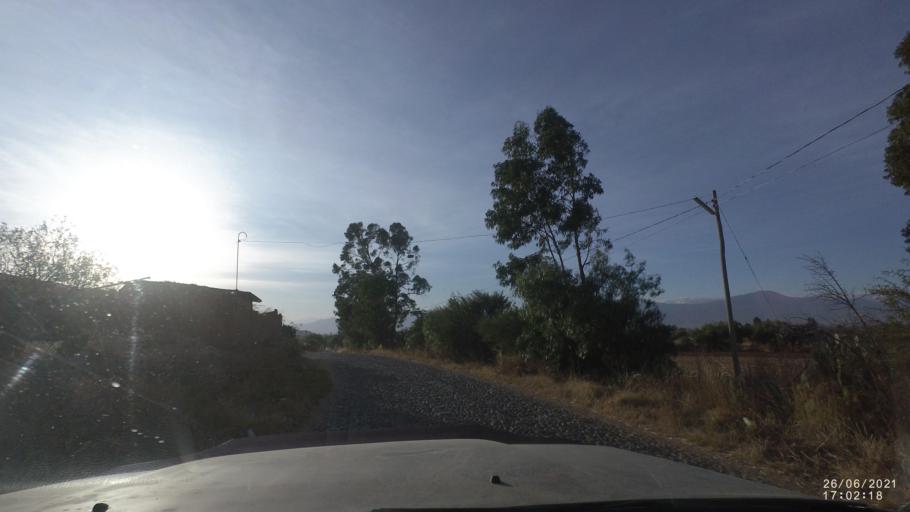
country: BO
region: Cochabamba
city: Cliza
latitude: -17.6545
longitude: -65.9120
